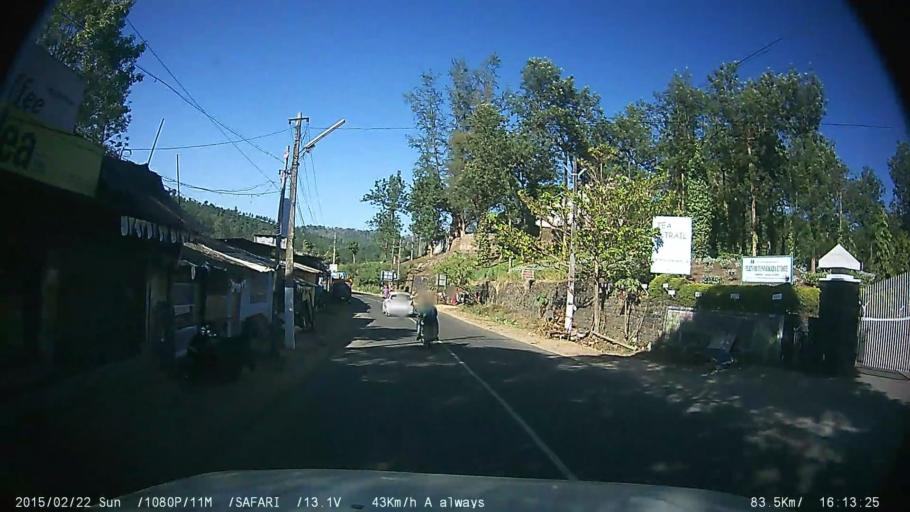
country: IN
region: Tamil Nadu
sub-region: Theni
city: Gudalur
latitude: 9.5780
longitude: 77.0970
